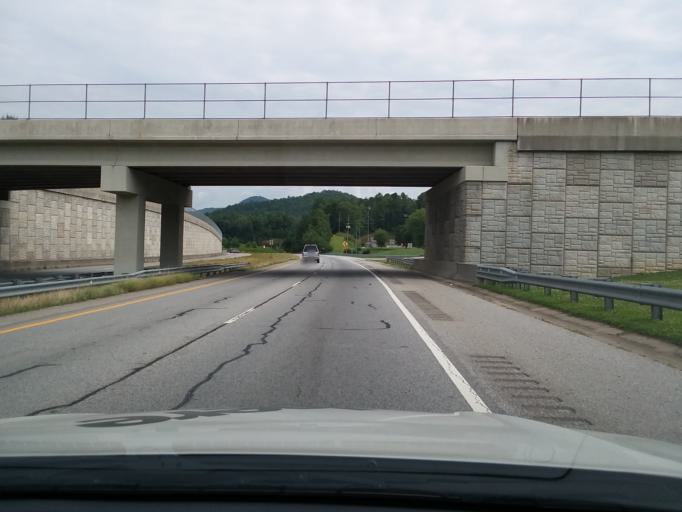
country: US
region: Georgia
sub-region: Rabun County
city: Clayton
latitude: 34.8264
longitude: -83.4246
